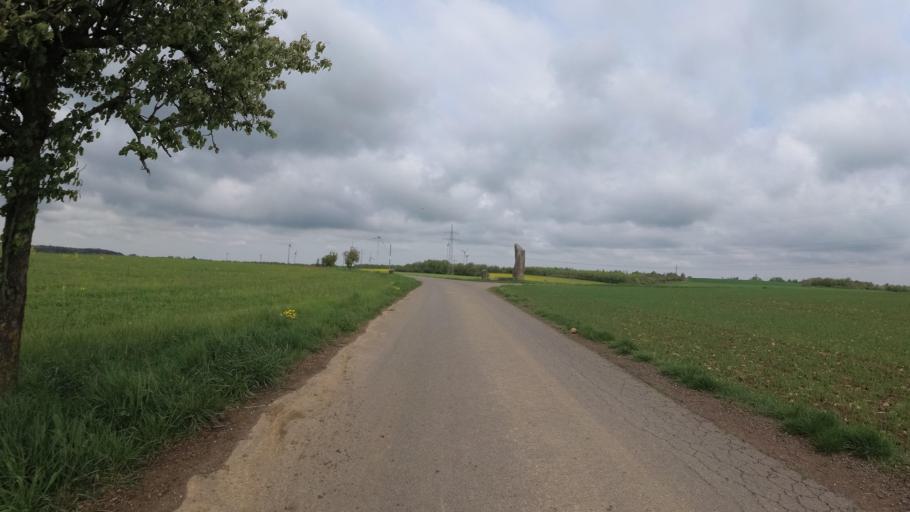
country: DE
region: Saarland
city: Orscholz
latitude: 49.4448
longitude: 6.5095
